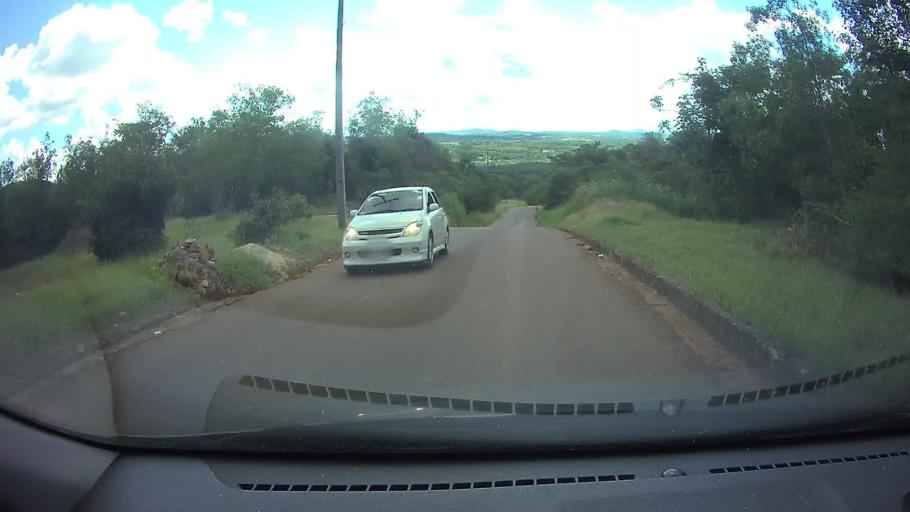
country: PY
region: Paraguari
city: La Colmena
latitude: -25.9286
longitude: -56.7871
